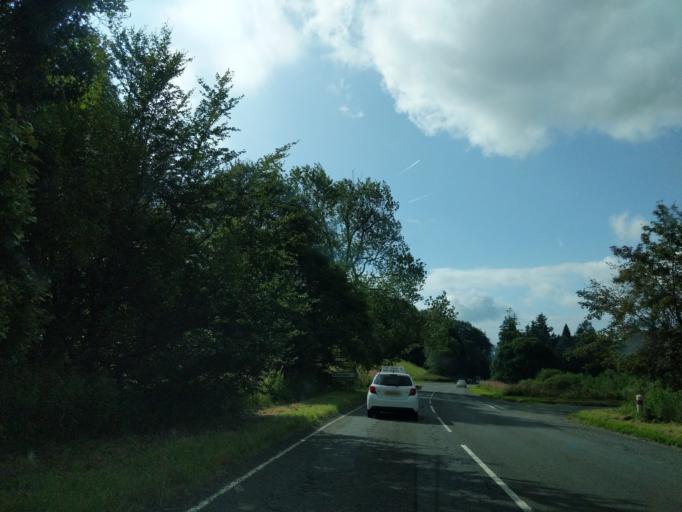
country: GB
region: Scotland
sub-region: Midlothian
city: Penicuik
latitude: 55.7469
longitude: -3.2045
